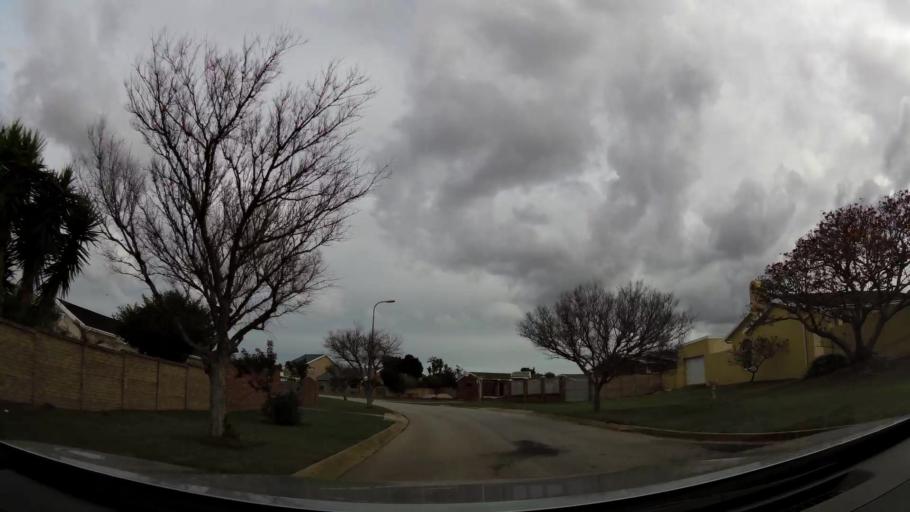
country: ZA
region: Eastern Cape
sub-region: Nelson Mandela Bay Metropolitan Municipality
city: Port Elizabeth
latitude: -33.9327
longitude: 25.5242
